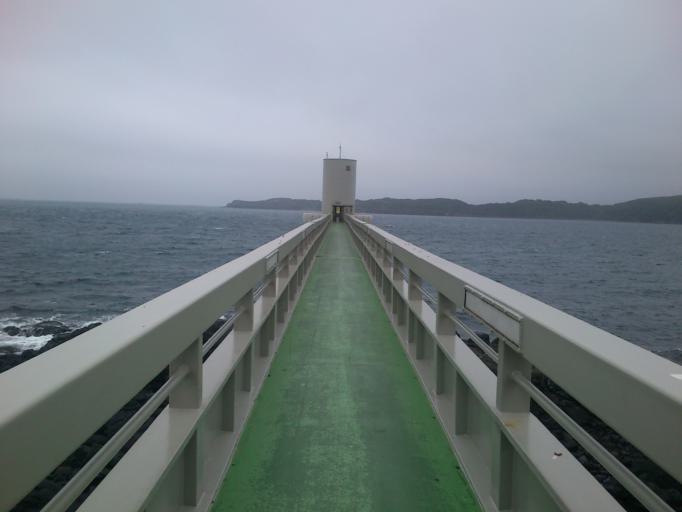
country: JP
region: Saga Prefecture
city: Karatsu
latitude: 33.5529
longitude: 129.8523
